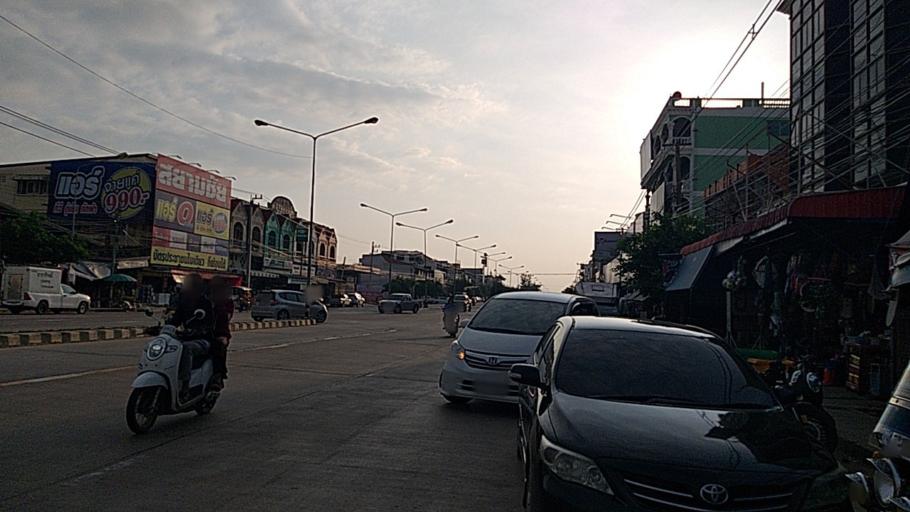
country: TH
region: Nakhon Ratchasima
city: Prathai
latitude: 15.5325
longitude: 102.7184
